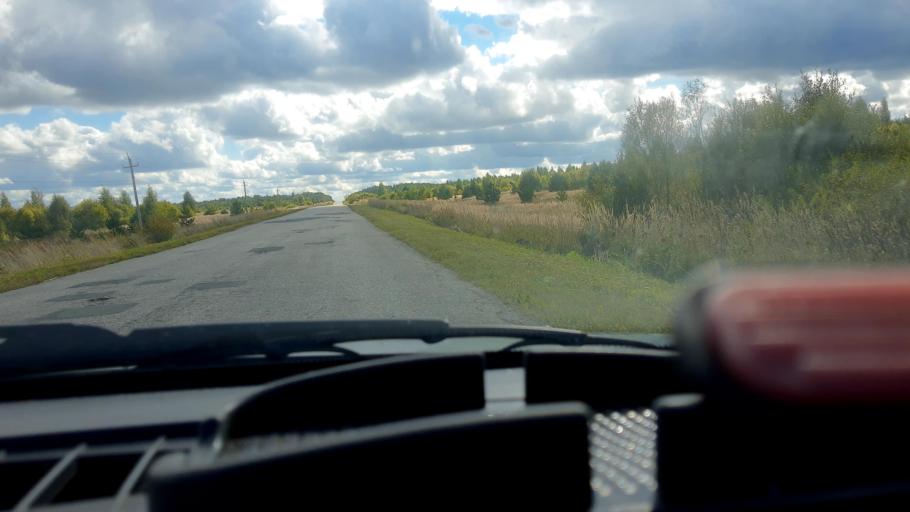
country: RU
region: Mariy-El
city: Kilemary
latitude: 56.9390
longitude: 46.6906
